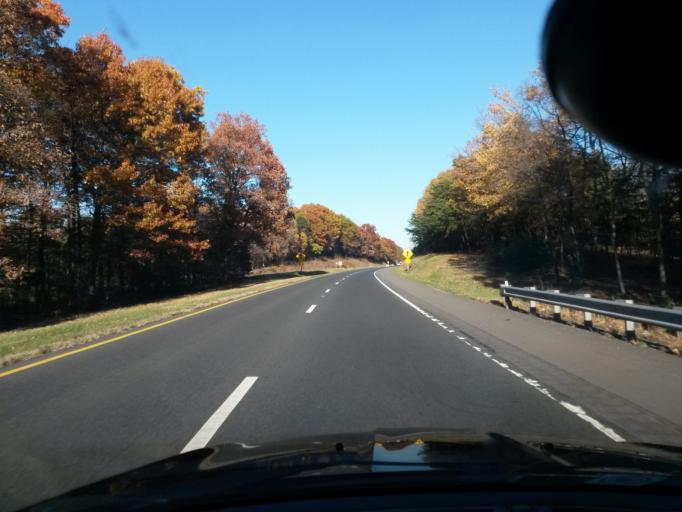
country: US
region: Virginia
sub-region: City of Lynchburg
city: West Lynchburg
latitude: 37.3610
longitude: -79.1650
